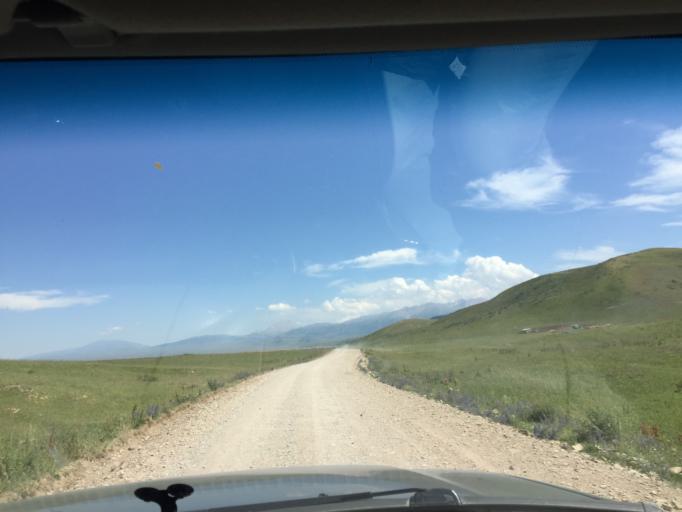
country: KZ
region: Almaty Oblysy
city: Kegen
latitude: 42.7699
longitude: 79.0833
